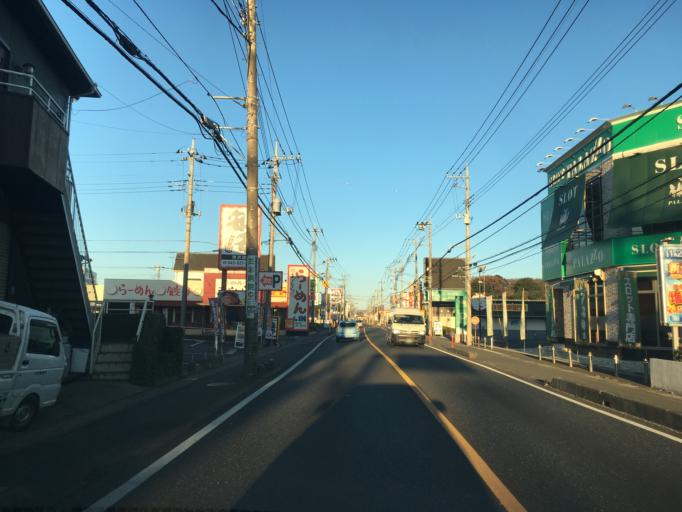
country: JP
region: Saitama
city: Tokorozawa
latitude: 35.8111
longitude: 139.4301
